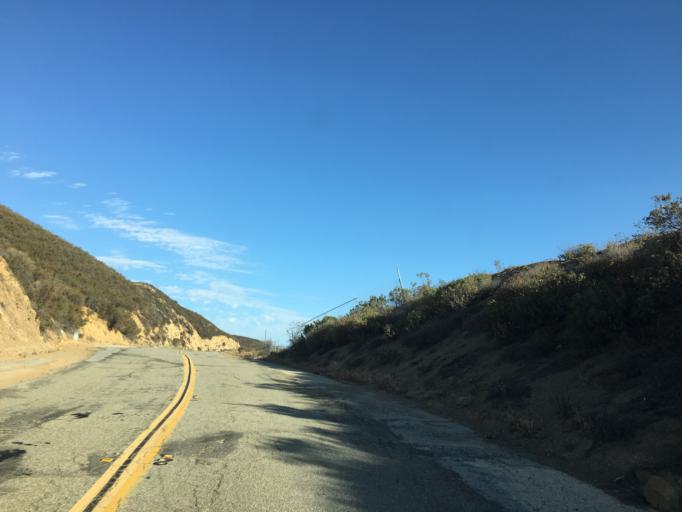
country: US
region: California
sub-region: Los Angeles County
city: Castaic
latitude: 34.5714
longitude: -118.6622
